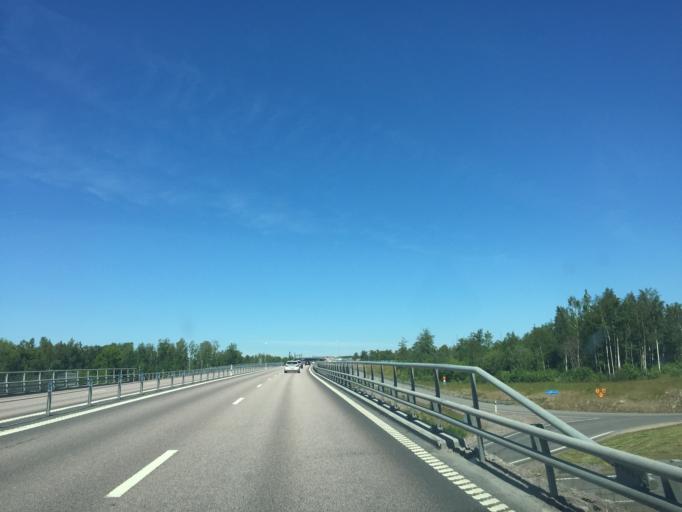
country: SE
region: OEstergoetland
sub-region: Motala Kommun
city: Motala
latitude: 58.5212
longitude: 15.0144
